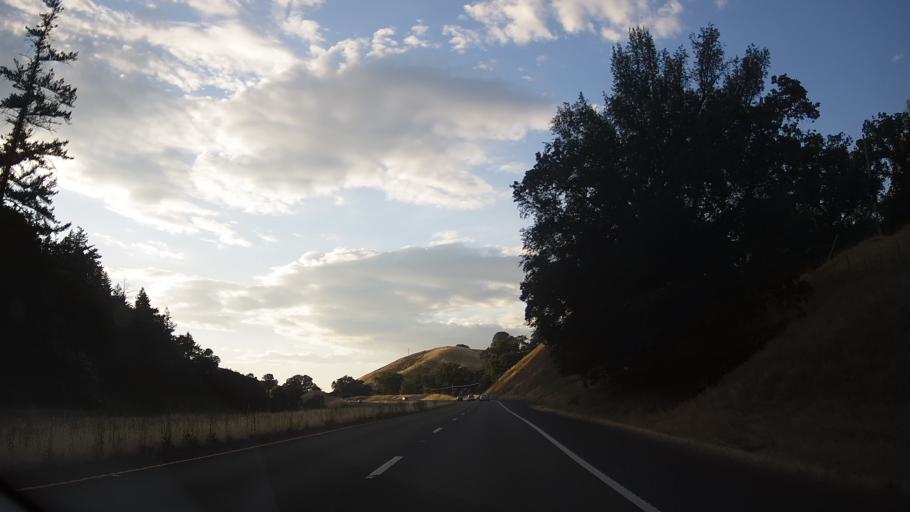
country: US
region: California
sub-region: Mendocino County
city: Talmage
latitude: 39.0680
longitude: -123.1681
